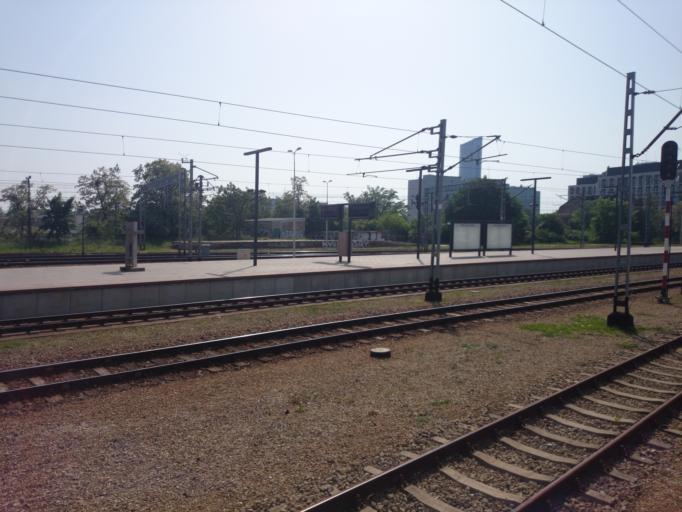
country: PL
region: Lower Silesian Voivodeship
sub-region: Powiat wroclawski
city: Wroclaw
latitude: 51.0983
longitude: 17.0357
